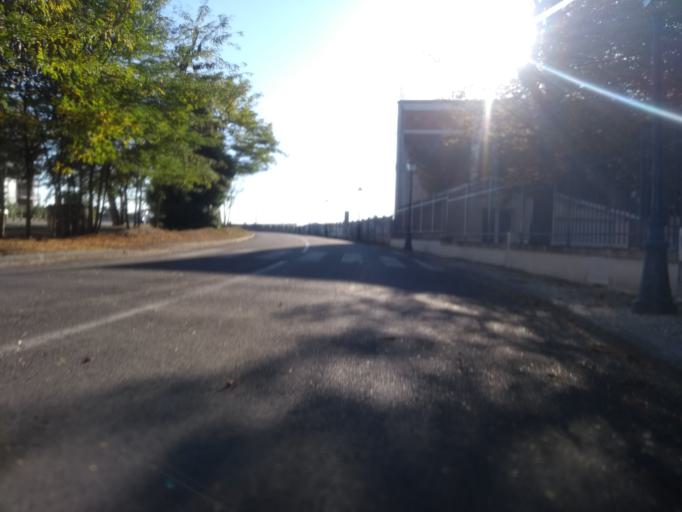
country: FR
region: Aquitaine
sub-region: Departement de la Gironde
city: Talence
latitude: 44.8175
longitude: -0.6022
